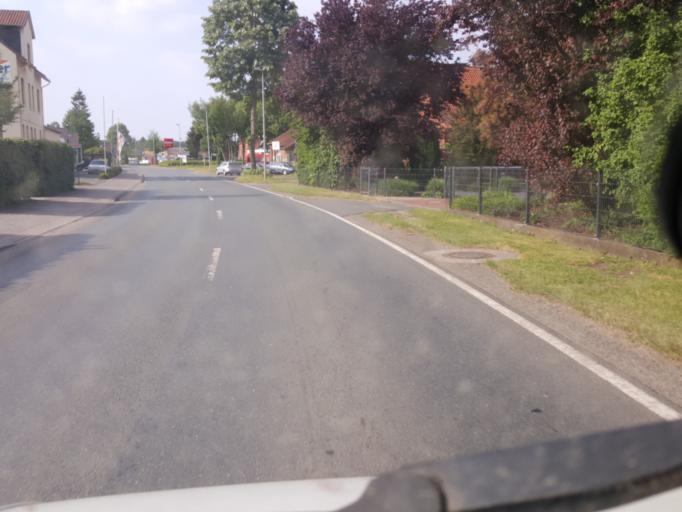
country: DE
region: Lower Saxony
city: Liebenau
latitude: 52.5987
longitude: 9.0995
